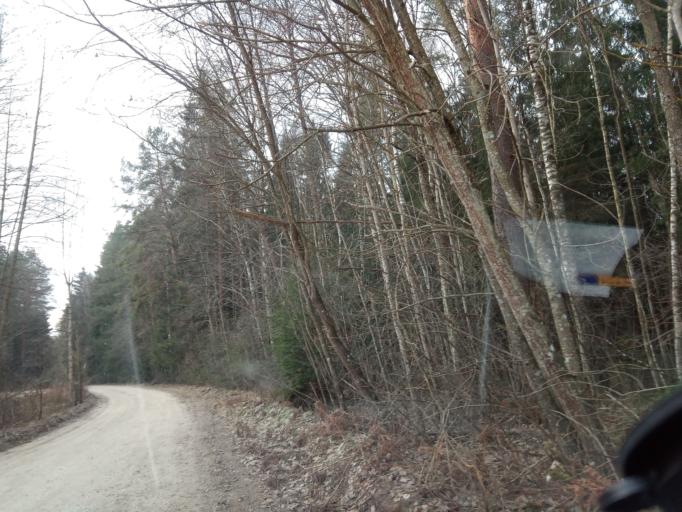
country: LT
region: Alytaus apskritis
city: Varena
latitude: 53.9911
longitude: 24.3469
